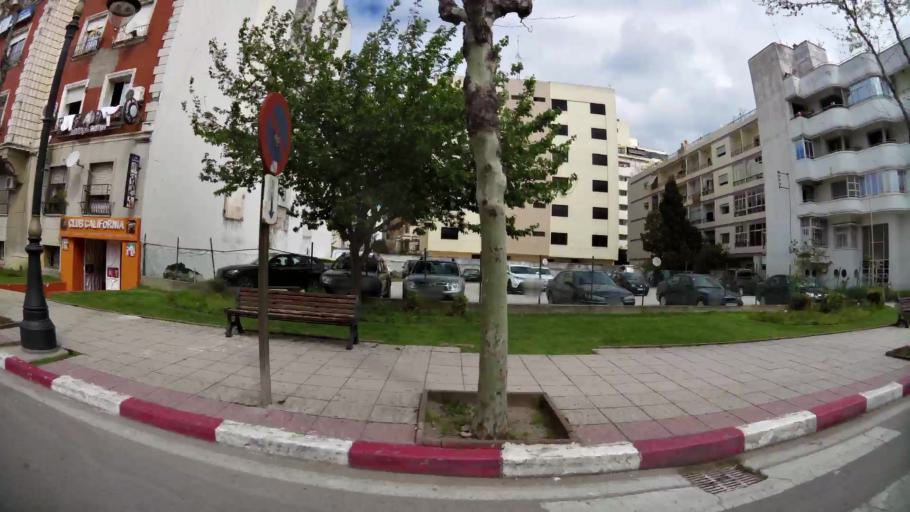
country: MA
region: Tanger-Tetouan
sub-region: Tanger-Assilah
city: Tangier
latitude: 35.7813
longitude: -5.8218
